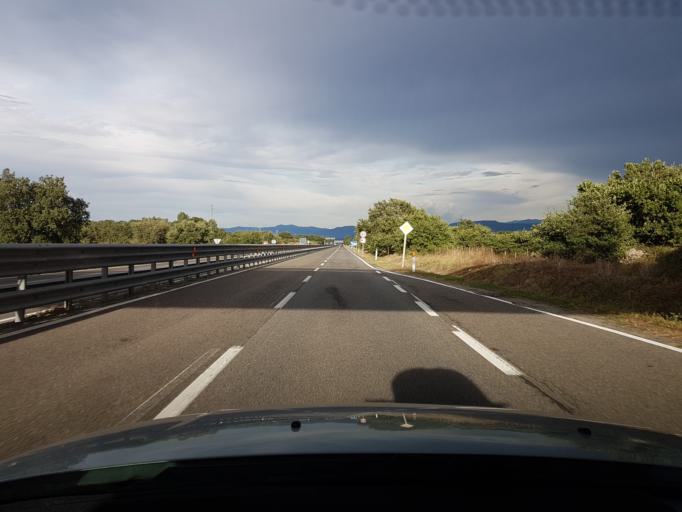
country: IT
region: Sardinia
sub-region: Provincia di Oristano
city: Abbasanta
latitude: 40.1146
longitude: 8.8185
